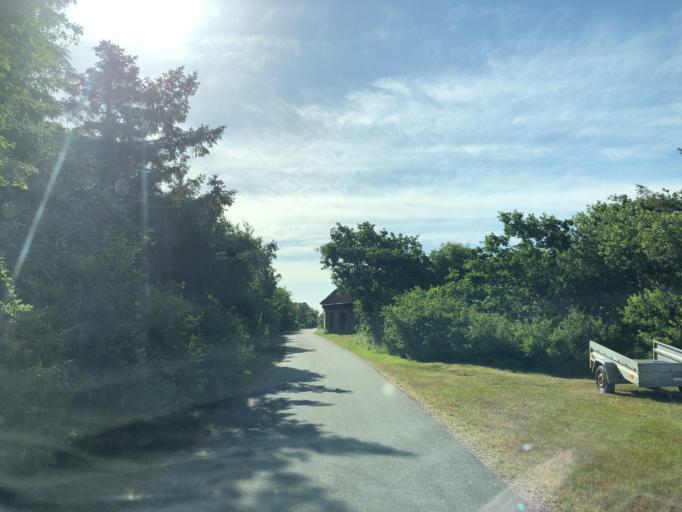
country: DK
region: Central Jutland
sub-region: Holstebro Kommune
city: Ulfborg
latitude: 56.3351
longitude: 8.2626
